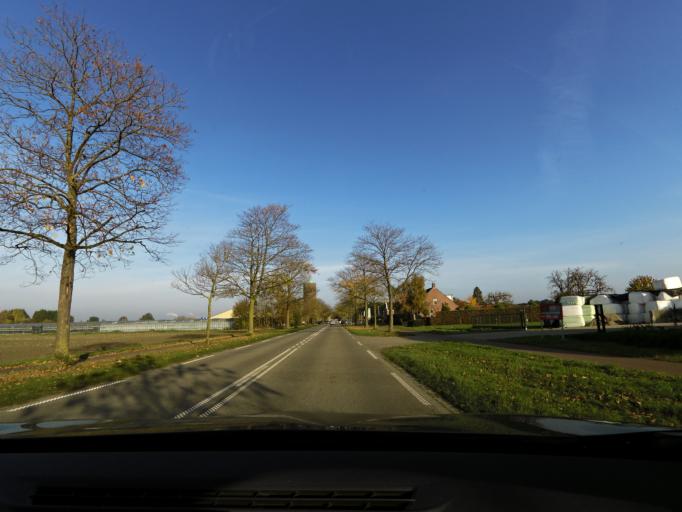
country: NL
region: North Brabant
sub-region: Gemeente Made en Drimmelen
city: Made
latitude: 51.6726
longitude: 4.7699
